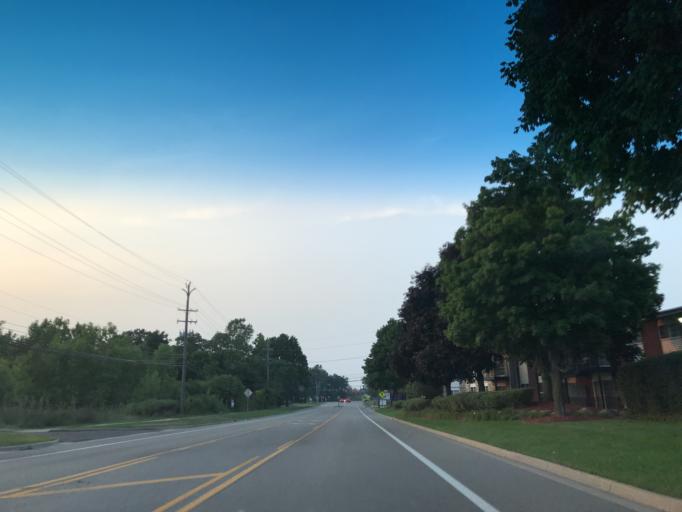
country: US
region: Michigan
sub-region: Washtenaw County
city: Ypsilanti
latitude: 42.2563
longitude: -83.6611
